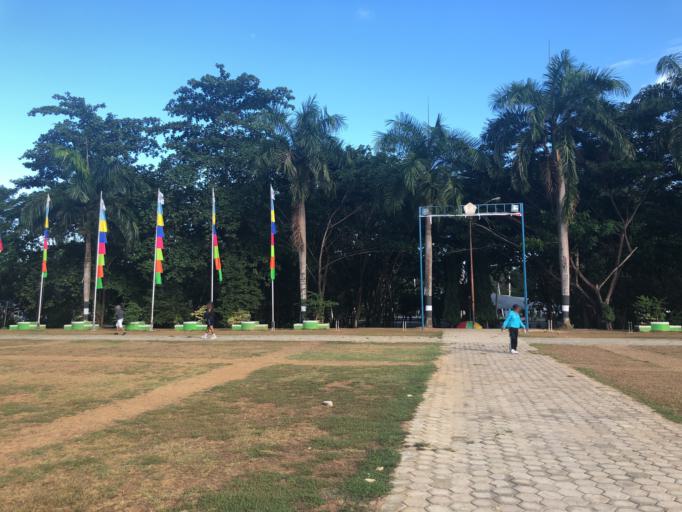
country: ID
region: Sulawesi Tenggara
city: Kendari
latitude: -3.9731
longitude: 122.5122
